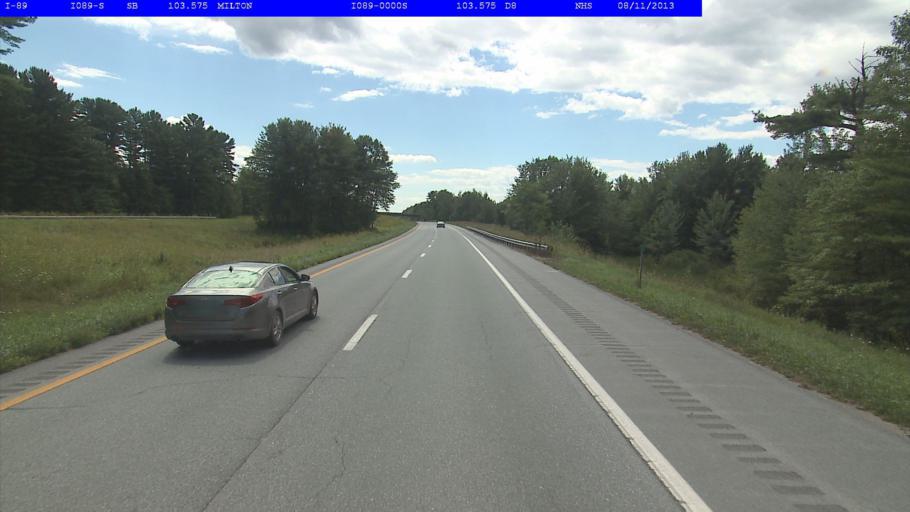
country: US
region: Vermont
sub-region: Chittenden County
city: Milton
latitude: 44.6651
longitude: -73.1368
